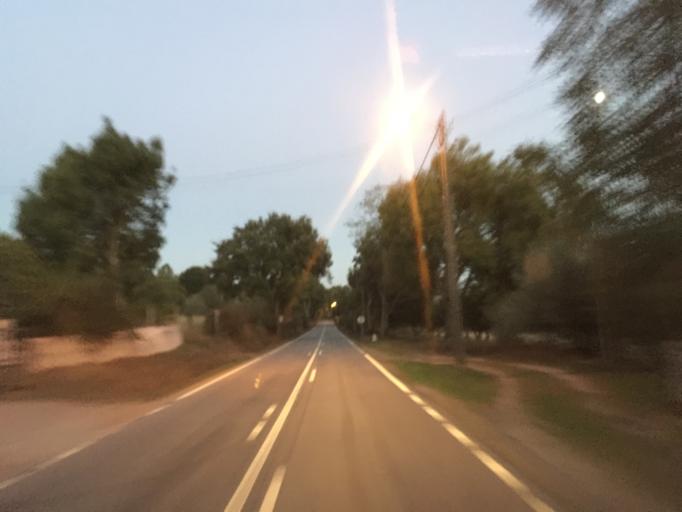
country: PT
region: Portalegre
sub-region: Castelo de Vide
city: Castelo de Vide
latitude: 39.3956
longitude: -7.4229
